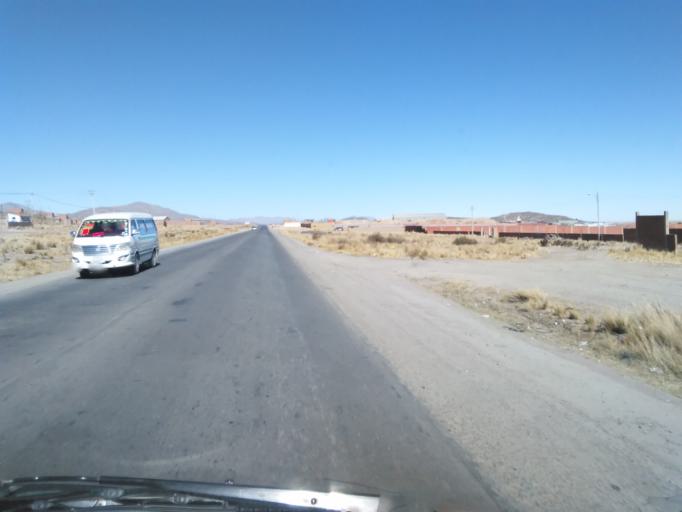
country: BO
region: Oruro
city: Oruro
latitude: -17.9918
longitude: -67.0474
